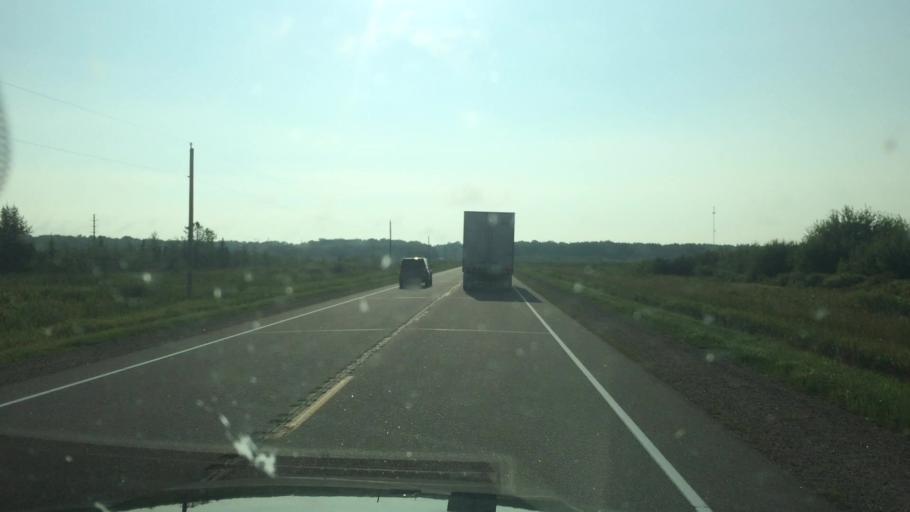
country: US
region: Wisconsin
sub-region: Langlade County
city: Antigo
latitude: 45.1471
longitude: -89.4027
